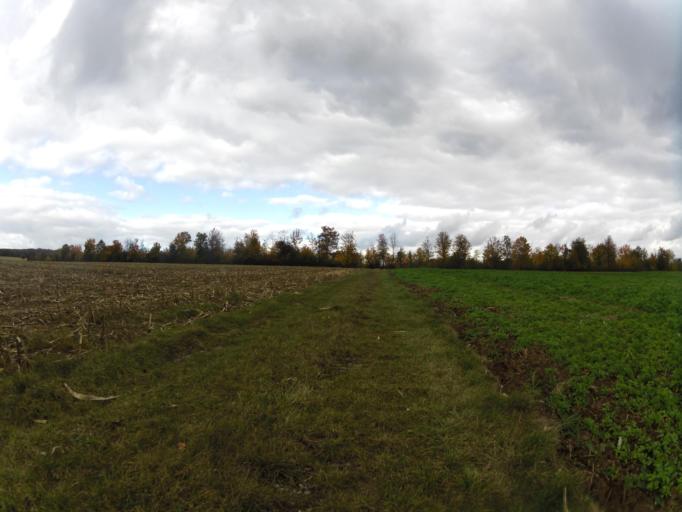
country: DE
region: Bavaria
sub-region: Regierungsbezirk Unterfranken
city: Kurnach
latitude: 49.8723
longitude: 10.0021
